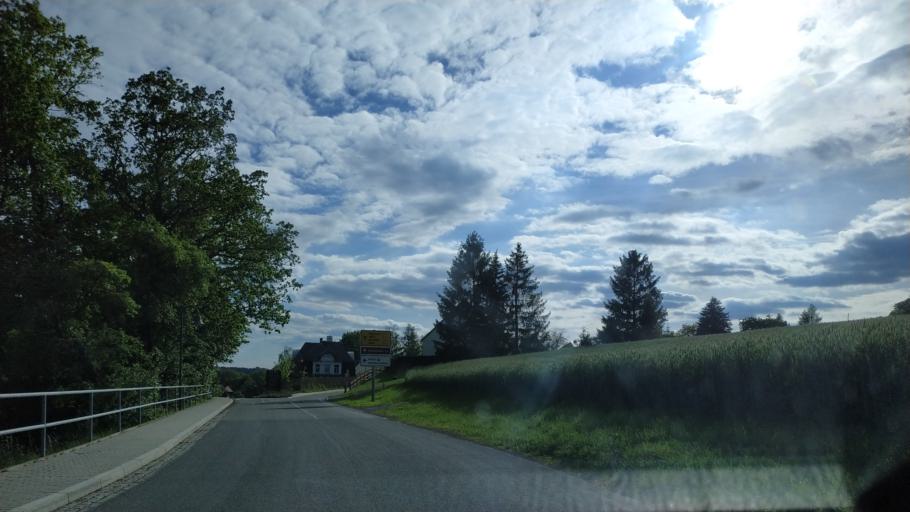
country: DE
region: Saxony
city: Pohl
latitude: 50.5597
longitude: 12.1782
